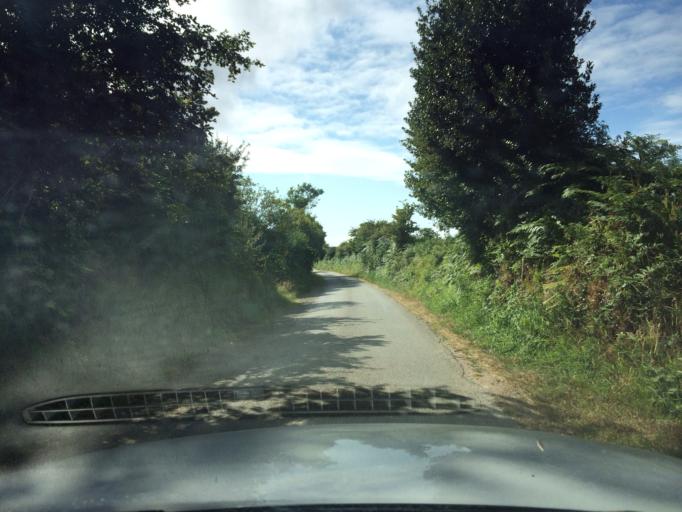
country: FR
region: Lower Normandy
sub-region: Departement de la Manche
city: Beaumont-Hague
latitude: 49.6869
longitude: -1.8748
